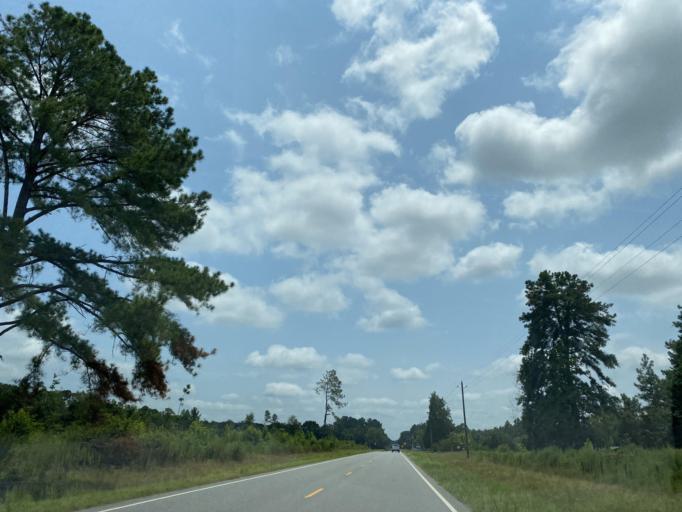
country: US
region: Georgia
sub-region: Jeff Davis County
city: Hazlehurst
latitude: 31.7910
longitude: -82.5650
